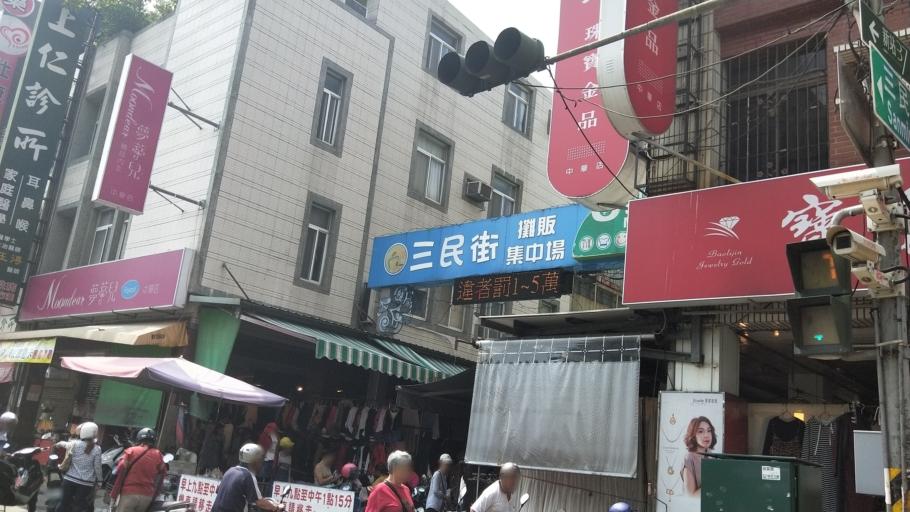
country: TW
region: Kaohsiung
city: Kaohsiung
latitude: 22.6362
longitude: 120.2932
